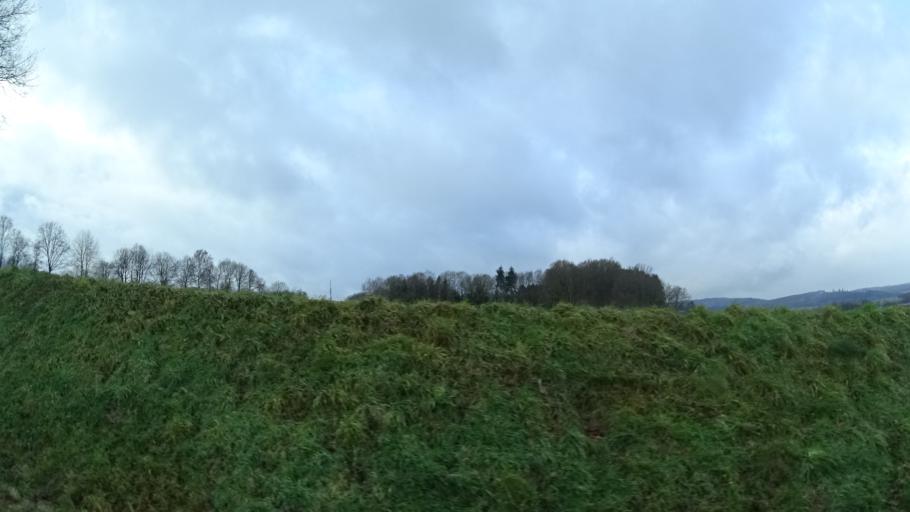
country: DE
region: Hesse
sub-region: Regierungsbezirk Kassel
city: Flieden
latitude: 50.4219
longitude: 9.5939
